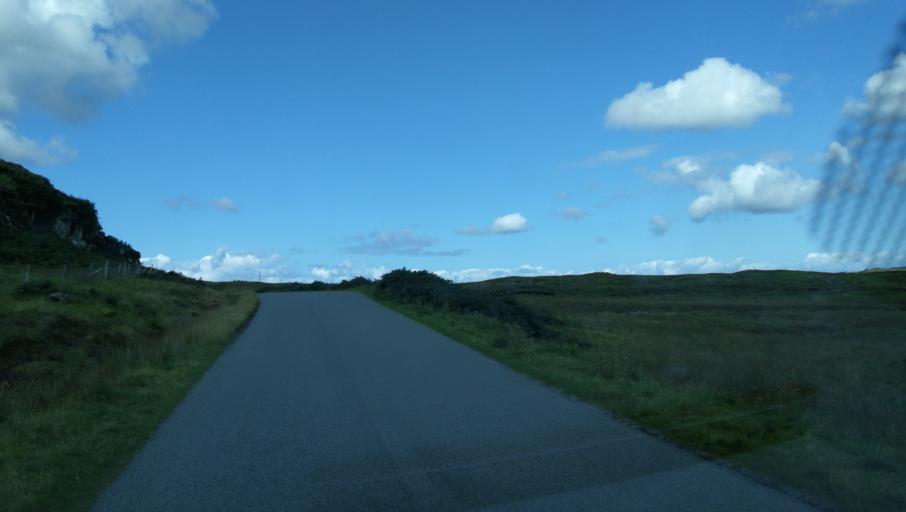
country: GB
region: Scotland
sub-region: Highland
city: Isle of Skye
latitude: 57.4238
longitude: -6.5953
